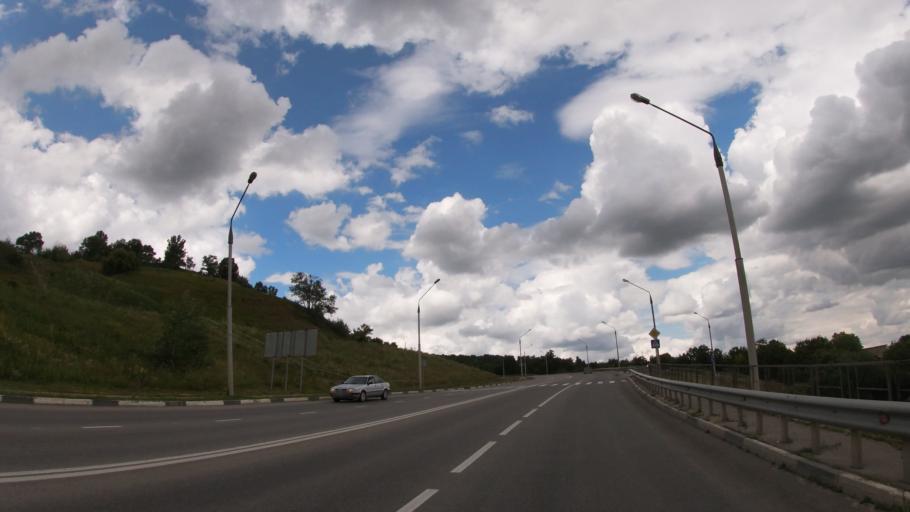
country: RU
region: Belgorod
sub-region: Belgorodskiy Rayon
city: Belgorod
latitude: 50.6185
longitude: 36.6163
